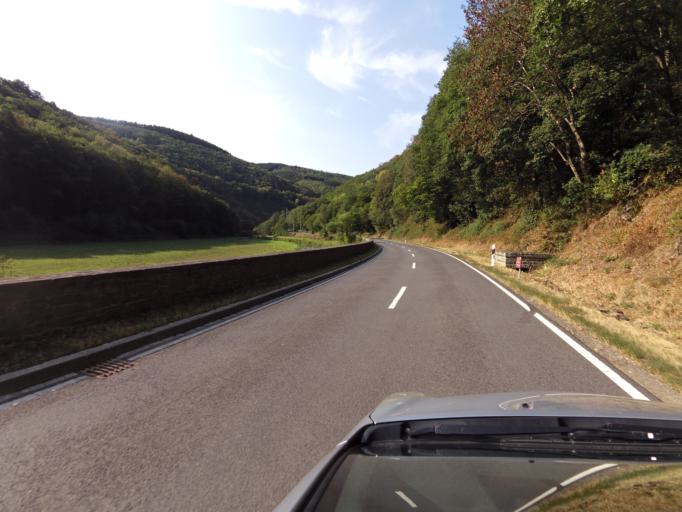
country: LU
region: Diekirch
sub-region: Canton de Diekirch
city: Bourscheid
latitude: 49.9241
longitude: 6.0635
